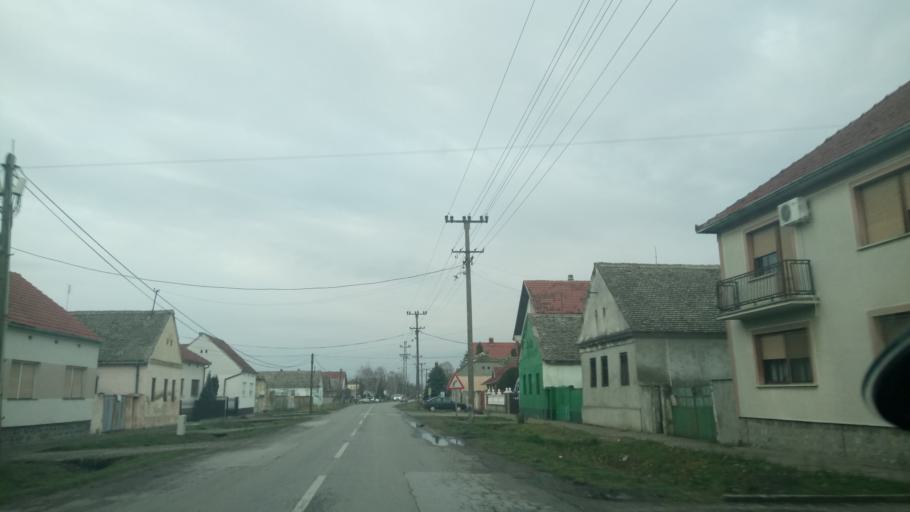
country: RS
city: Vojka
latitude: 44.9434
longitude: 20.1534
